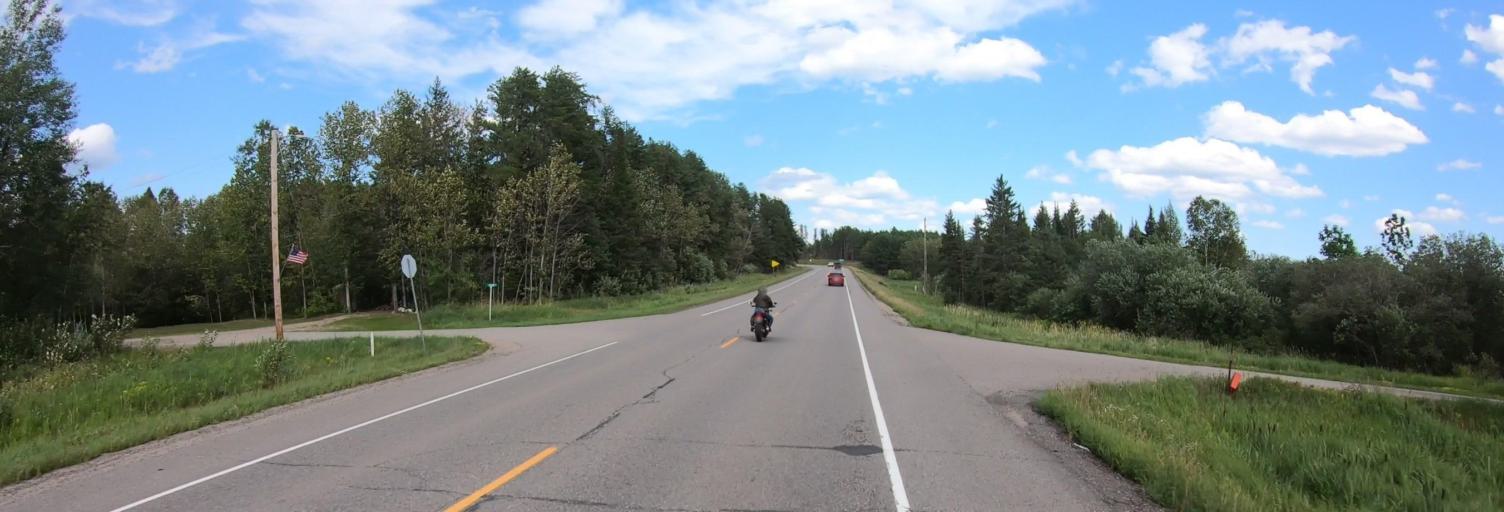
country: US
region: Minnesota
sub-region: Saint Louis County
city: Aurora
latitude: 47.8130
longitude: -92.2354
